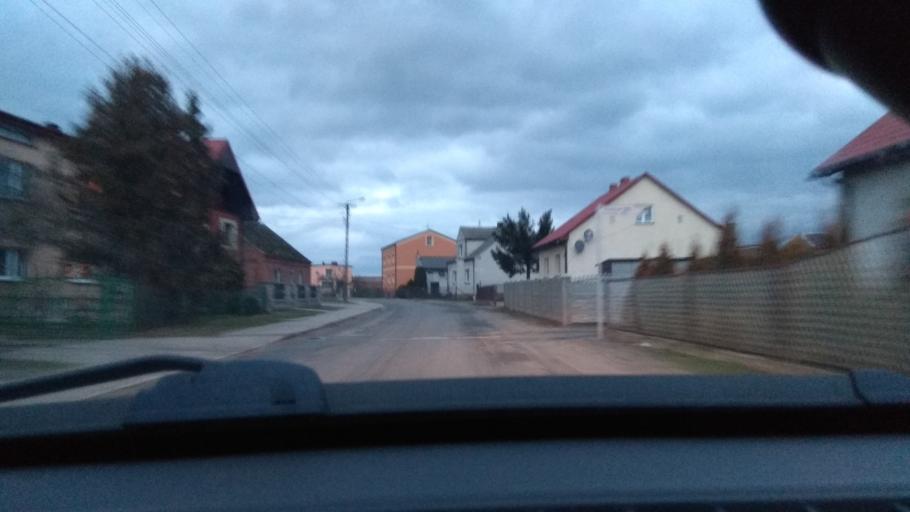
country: PL
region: Lodz Voivodeship
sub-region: Powiat wieruszowski
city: Wieruszow
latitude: 51.3049
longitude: 18.0814
